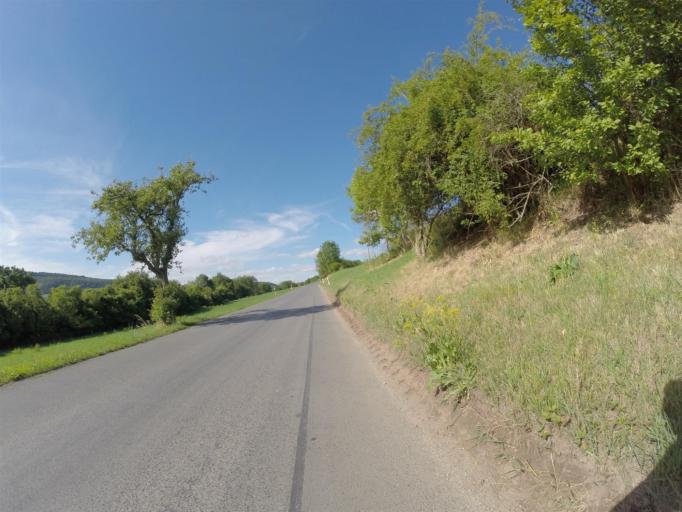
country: DE
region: Thuringia
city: Neuengonna
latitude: 50.9598
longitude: 11.6408
